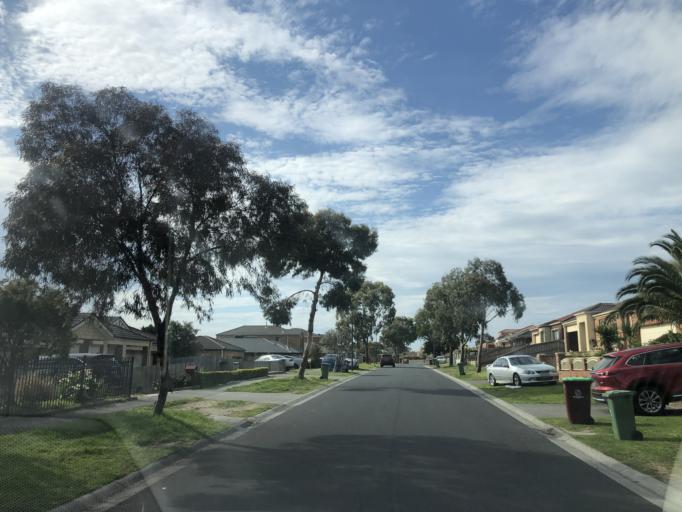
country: AU
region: Victoria
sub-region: Casey
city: Hampton Park
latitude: -38.0435
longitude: 145.2565
